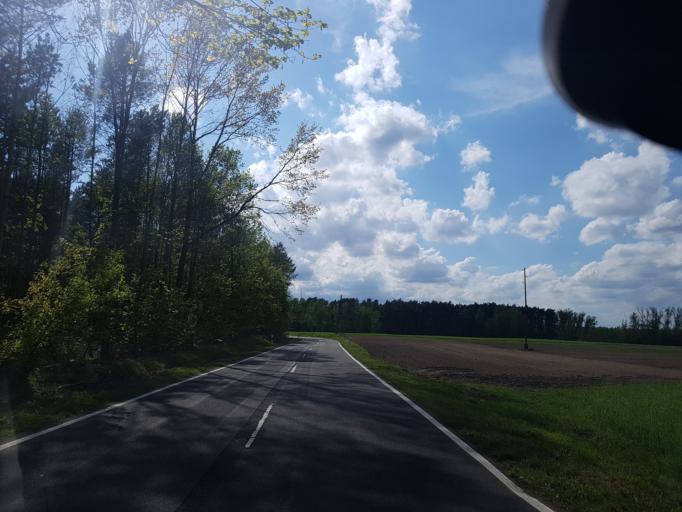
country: DE
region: Brandenburg
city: Drebkau
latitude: 51.6548
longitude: 14.3171
